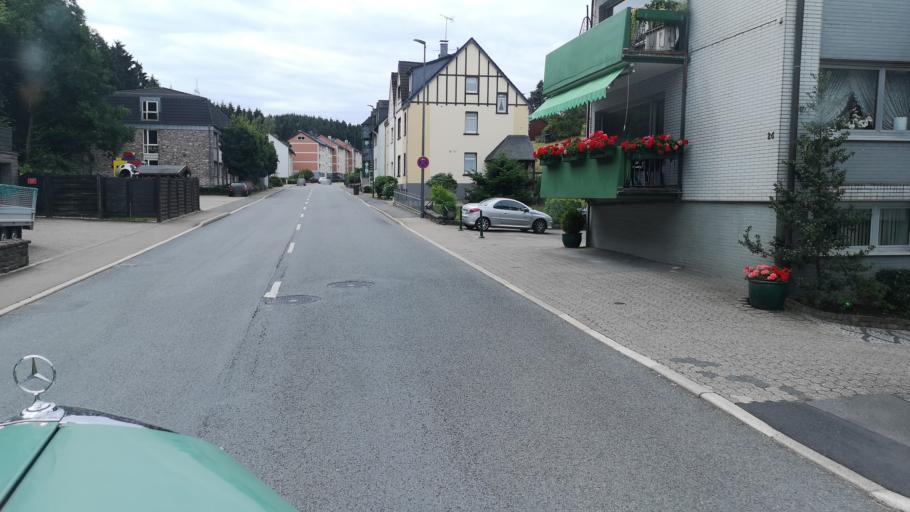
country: DE
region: North Rhine-Westphalia
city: Wipperfurth
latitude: 51.1122
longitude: 7.3877
